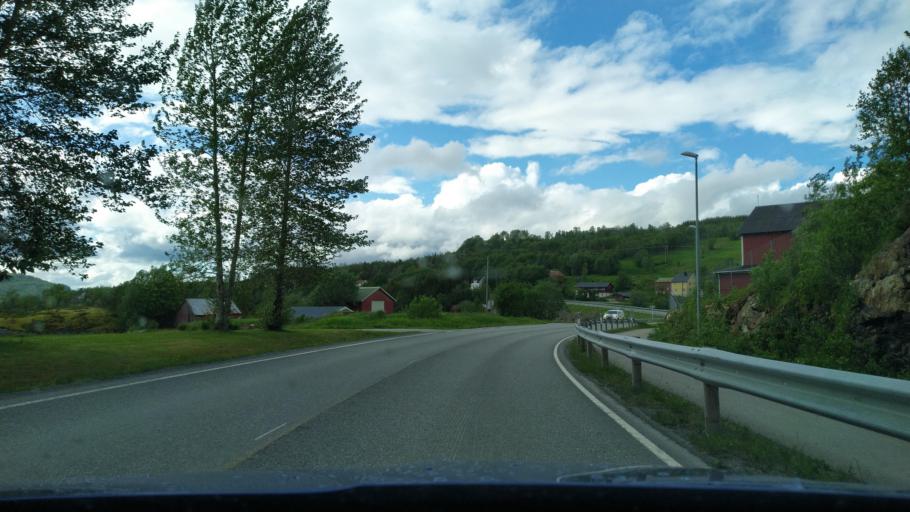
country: NO
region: Troms
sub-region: Sorreisa
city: Sorreisa
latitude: 69.1747
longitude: 18.0835
